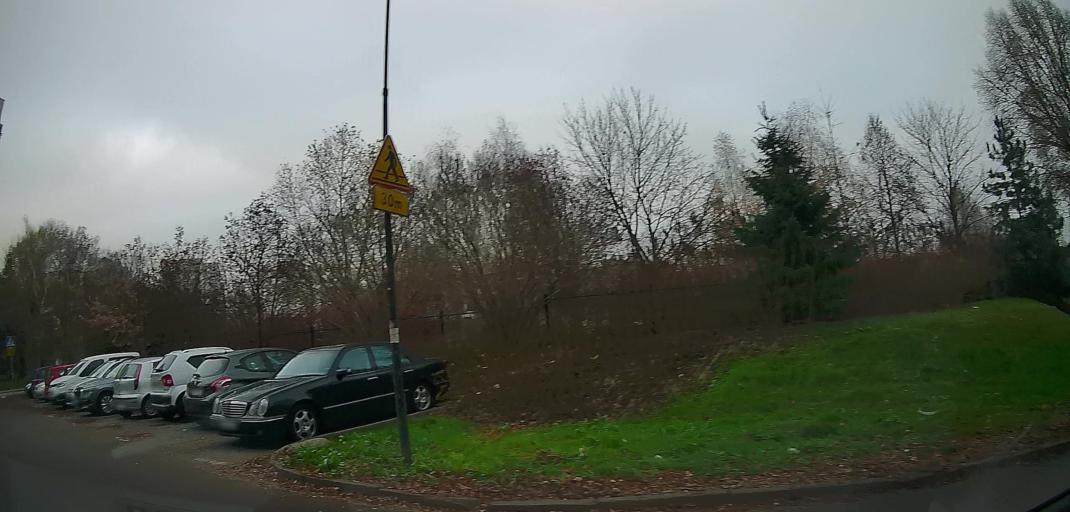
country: PL
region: Masovian Voivodeship
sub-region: Warszawa
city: Ursynow
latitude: 52.1572
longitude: 21.0268
